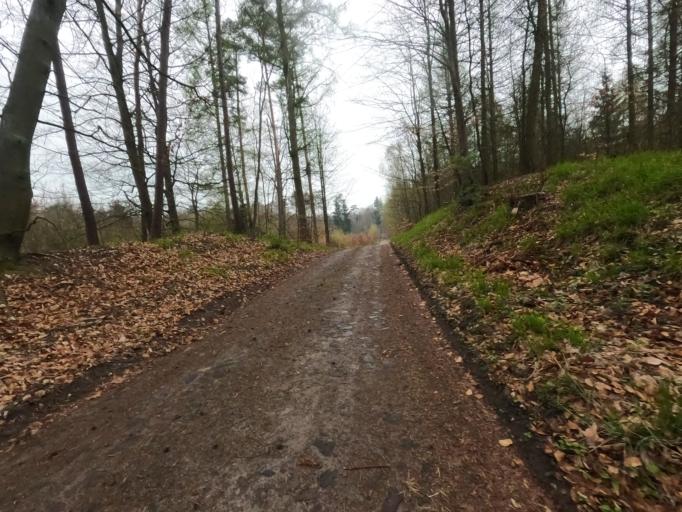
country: PL
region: West Pomeranian Voivodeship
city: Trzcinsko Zdroj
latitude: 52.9257
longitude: 14.7005
